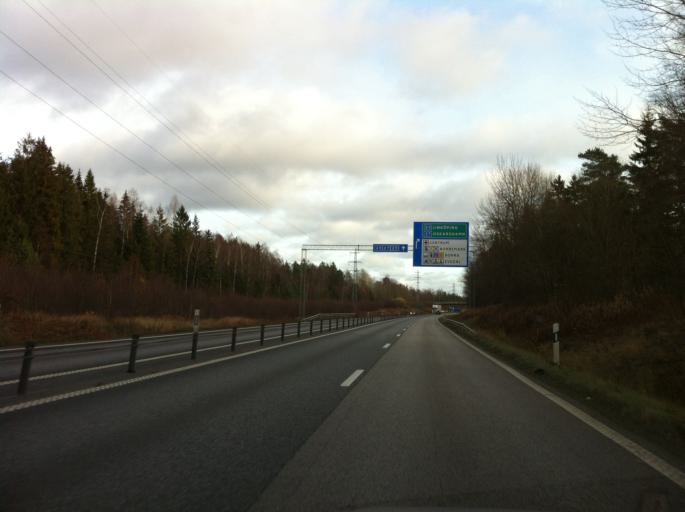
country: SE
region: Kronoberg
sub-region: Vaxjo Kommun
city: Gemla
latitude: 56.8380
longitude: 14.7054
